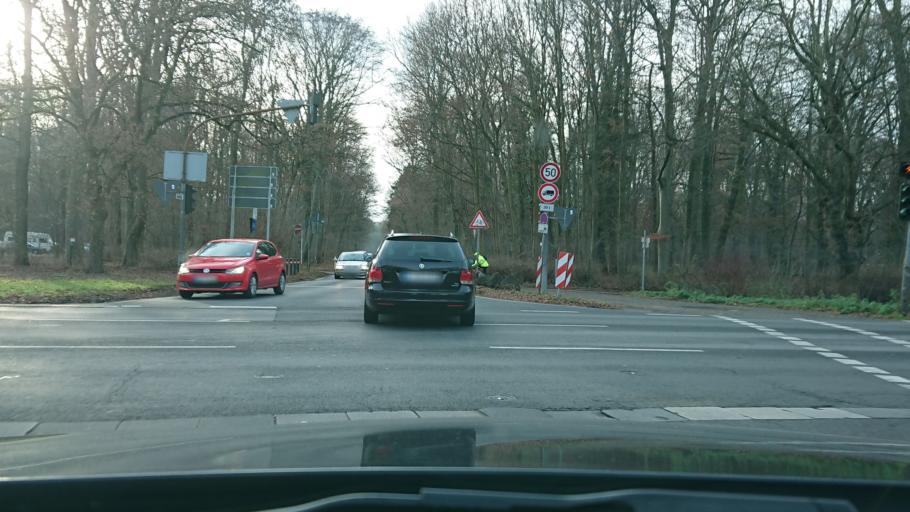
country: DE
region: North Rhine-Westphalia
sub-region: Regierungsbezirk Koln
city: Hurth
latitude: 50.9148
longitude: 6.8958
